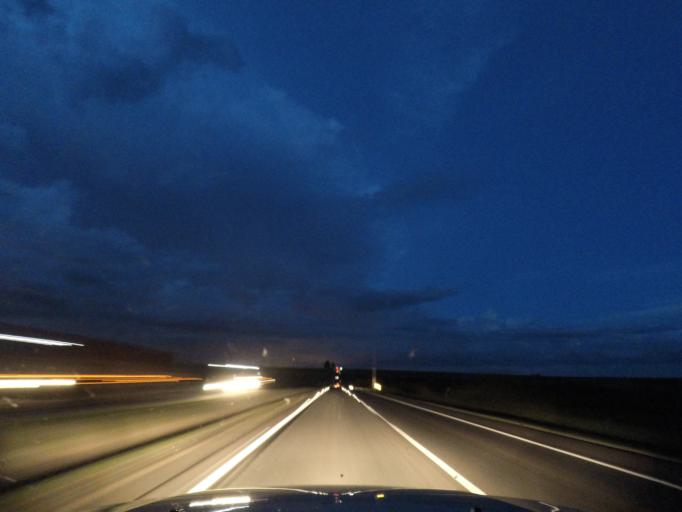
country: BR
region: Minas Gerais
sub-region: Uberlandia
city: Uberlandia
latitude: -19.2058
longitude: -48.1500
